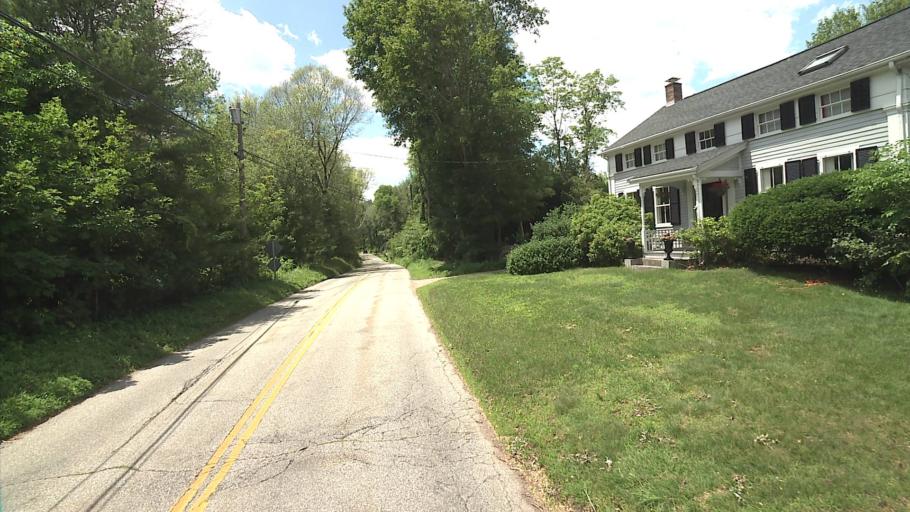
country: US
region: Connecticut
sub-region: New London County
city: Old Mystic
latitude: 41.4445
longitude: -71.9021
